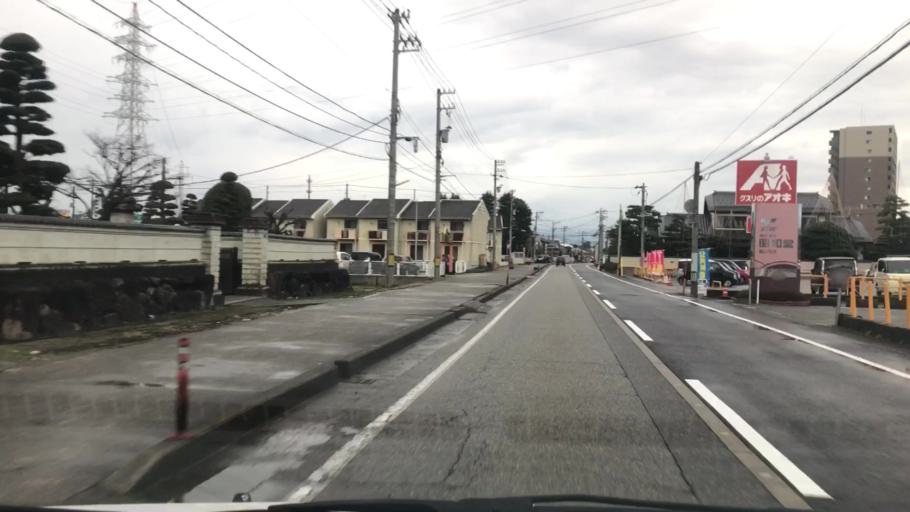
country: JP
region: Toyama
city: Toyama-shi
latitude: 36.6641
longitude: 137.2110
